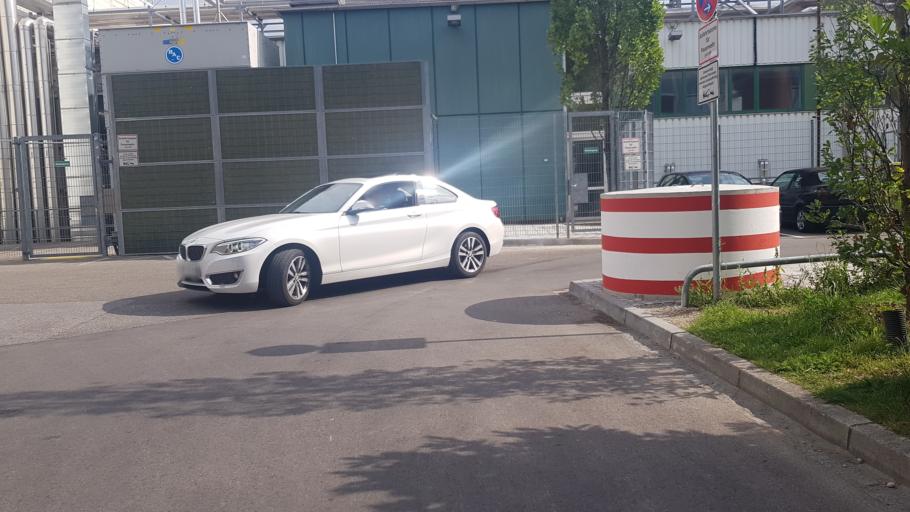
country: DE
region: Bavaria
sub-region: Upper Bavaria
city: Pullach im Isartal
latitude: 48.1015
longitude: 11.5318
